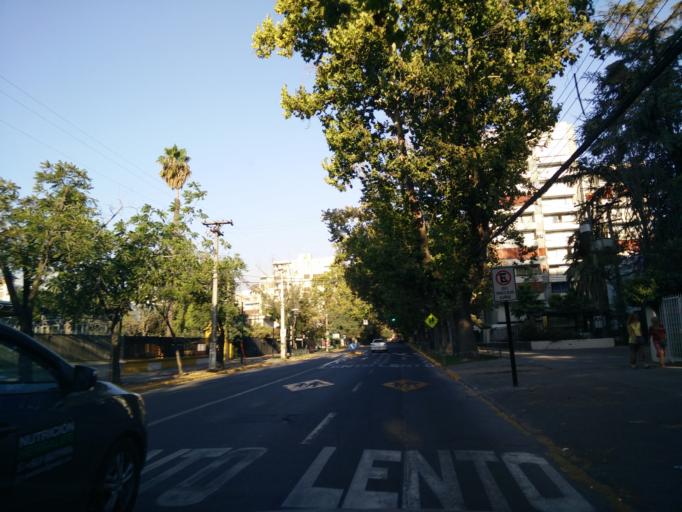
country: CL
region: Santiago Metropolitan
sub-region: Provincia de Santiago
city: Villa Presidente Frei, Nunoa, Santiago, Chile
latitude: -33.4573
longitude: -70.6042
